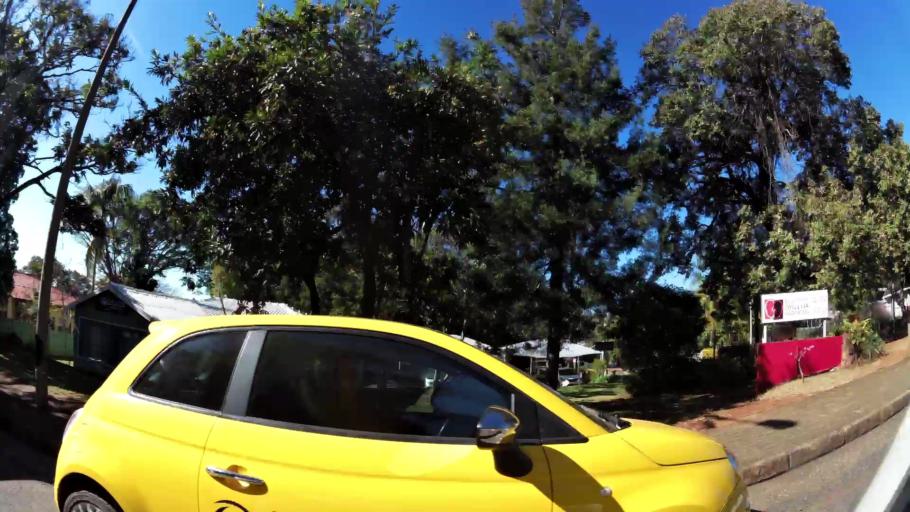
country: ZA
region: Limpopo
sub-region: Mopani District Municipality
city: Tzaneen
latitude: -23.8331
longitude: 30.1566
